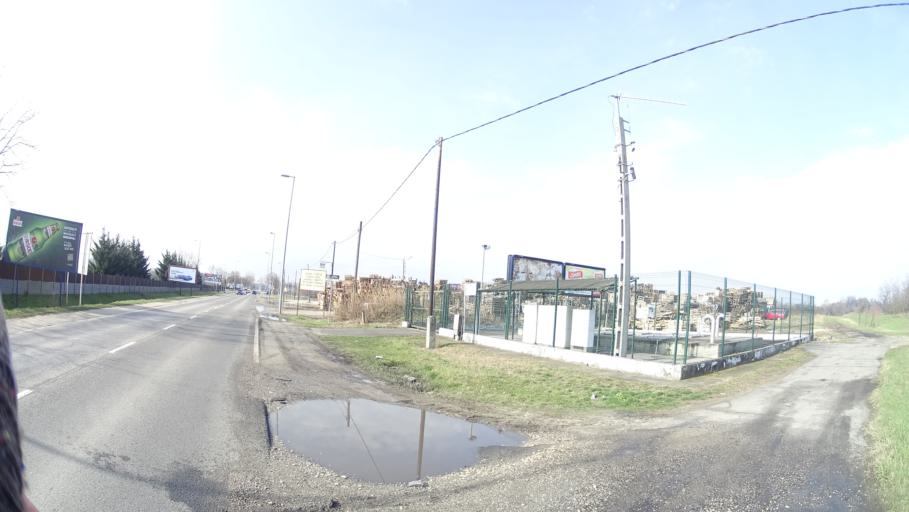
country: HU
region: Budapest
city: Budapest XXIII. keruelet
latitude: 47.4172
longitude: 19.1448
